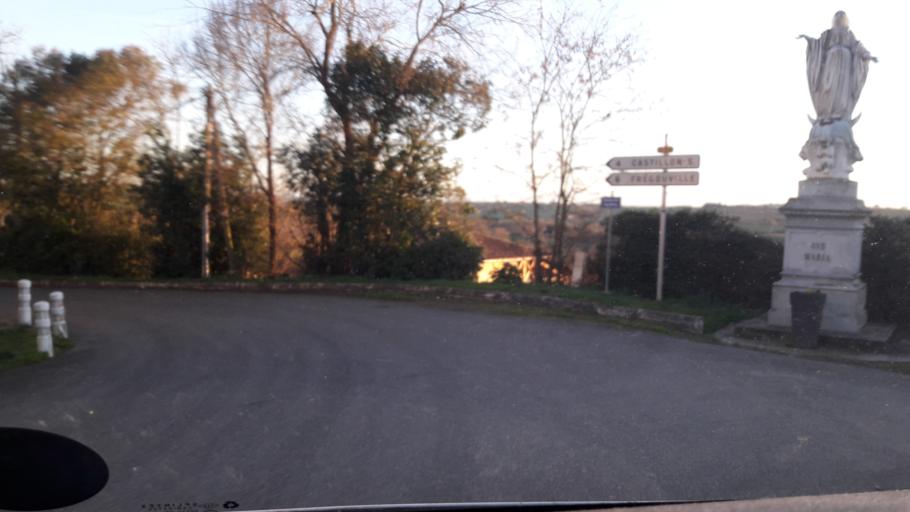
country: FR
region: Midi-Pyrenees
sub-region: Departement du Gers
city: Gimont
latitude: 43.5977
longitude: 0.9810
